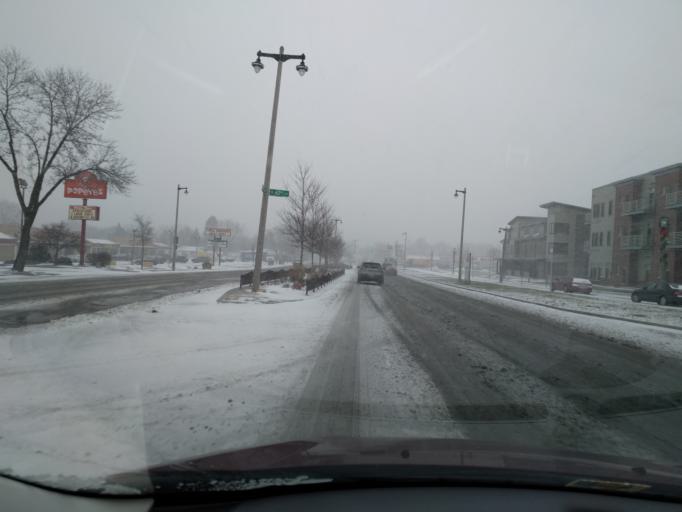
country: US
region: Wisconsin
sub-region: Milwaukee County
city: Brown Deer
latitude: 43.1193
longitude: -87.9885
